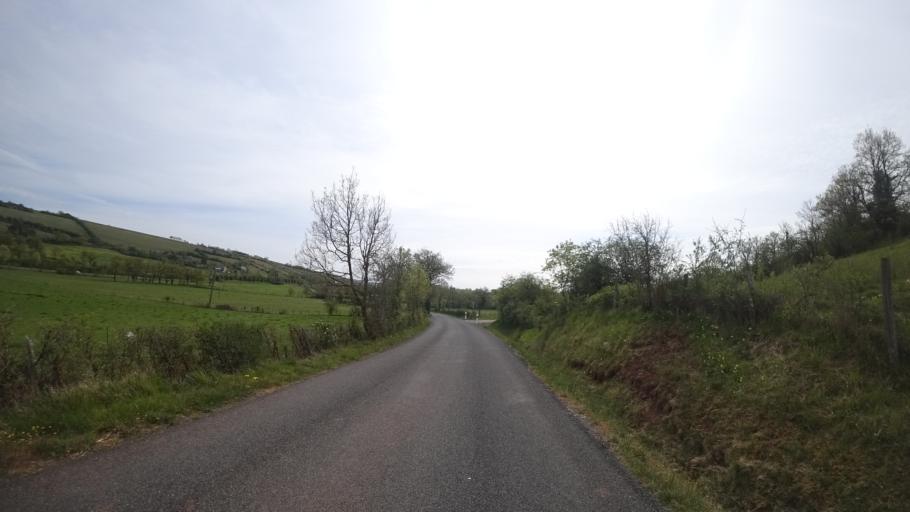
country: FR
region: Midi-Pyrenees
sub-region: Departement de l'Aveyron
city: Sebazac-Concoures
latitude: 44.3728
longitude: 2.6144
